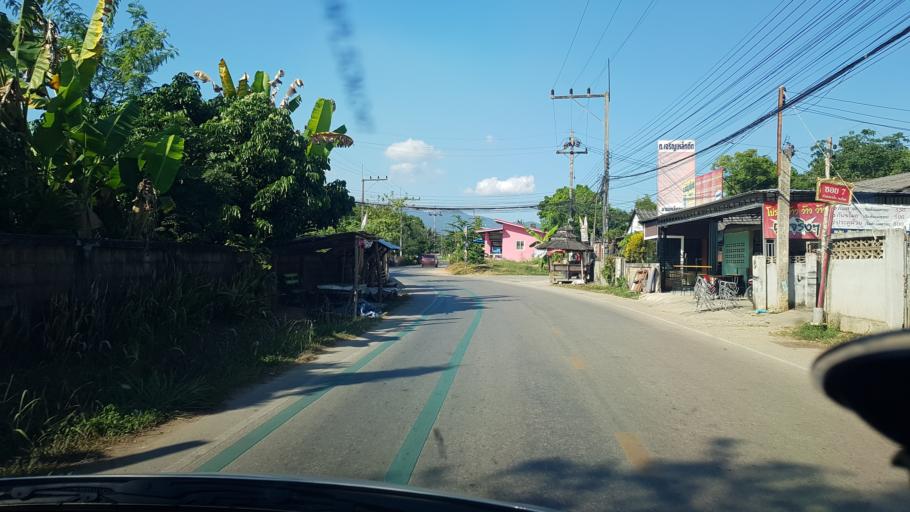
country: TH
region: Chiang Rai
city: Chiang Rai
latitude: 19.9451
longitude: 99.8106
